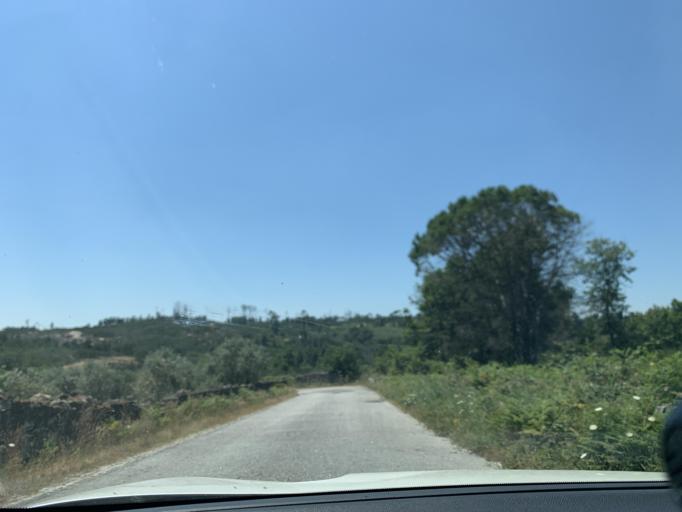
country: PT
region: Viseu
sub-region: Mangualde
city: Mangualde
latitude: 40.5550
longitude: -7.7328
